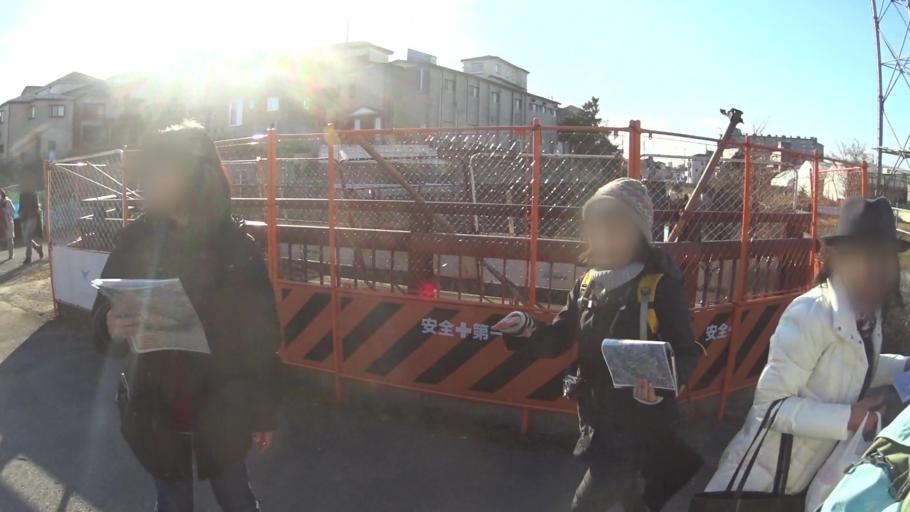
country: JP
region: Saitama
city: Shimotoda
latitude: 35.8467
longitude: 139.6912
